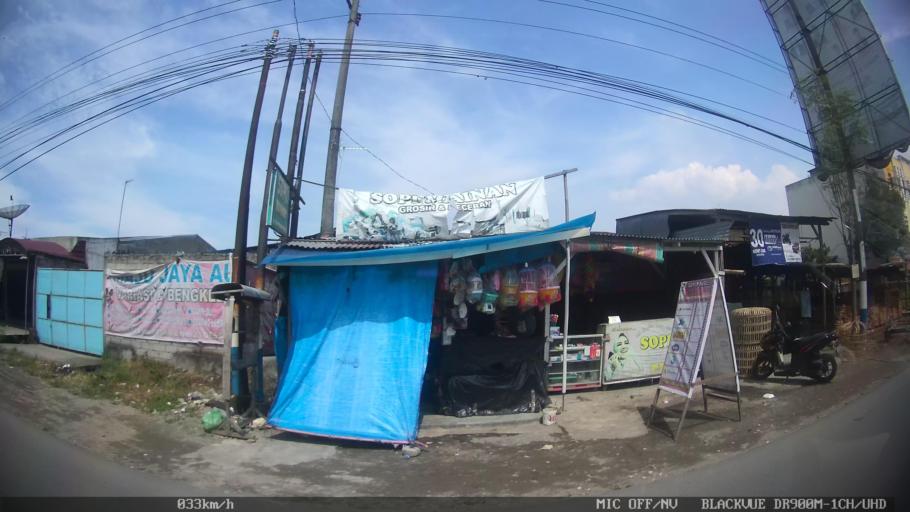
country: ID
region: North Sumatra
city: Labuhan Deli
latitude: 3.6622
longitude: 98.6565
